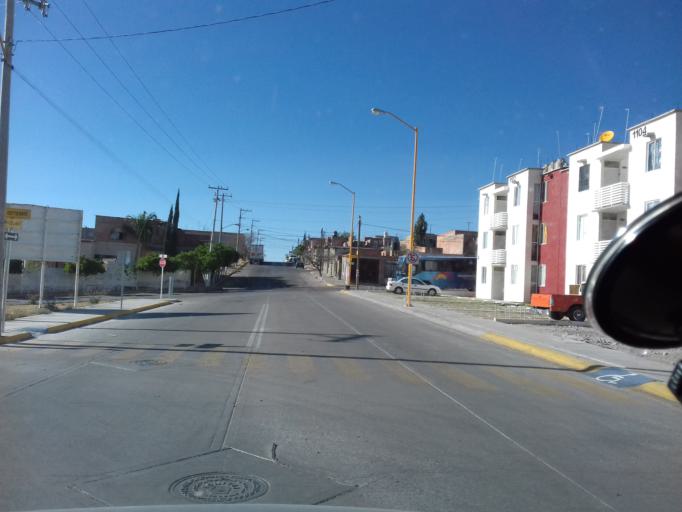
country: MX
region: Aguascalientes
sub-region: Aguascalientes
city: San Sebastian [Fraccionamiento]
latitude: 21.8488
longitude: -102.2641
